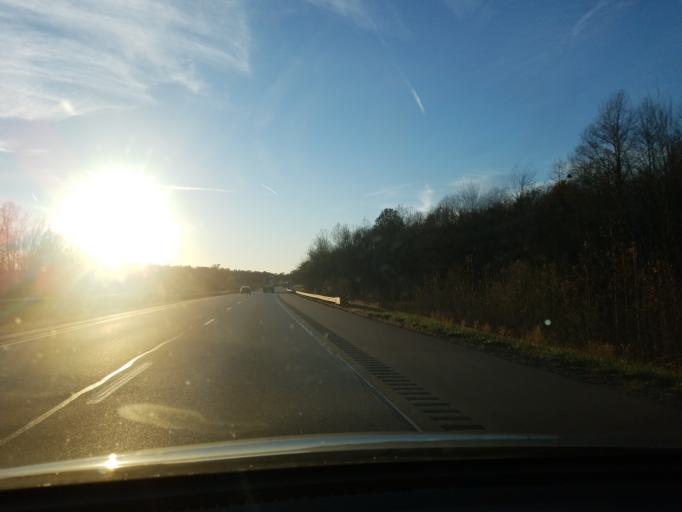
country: US
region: Indiana
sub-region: Warrick County
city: Chandler
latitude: 38.1853
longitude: -87.3624
